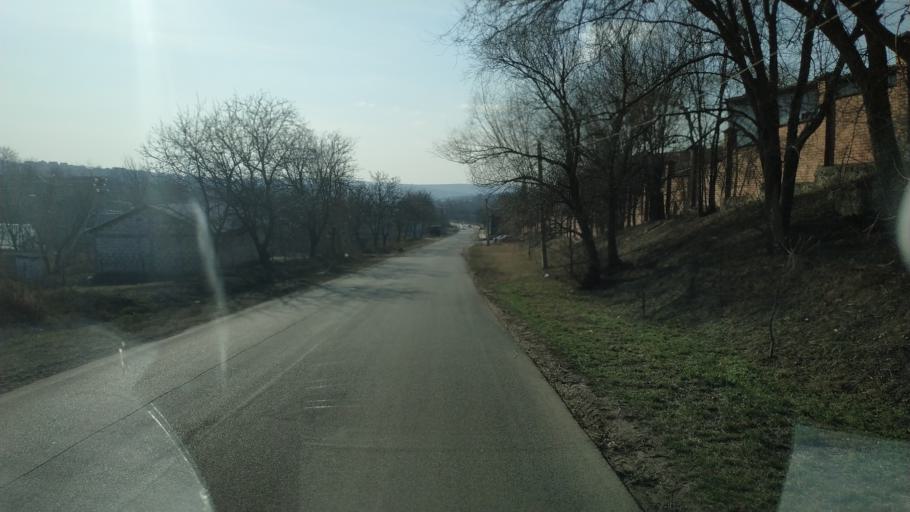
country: MD
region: Chisinau
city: Singera
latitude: 46.8397
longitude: 29.0276
